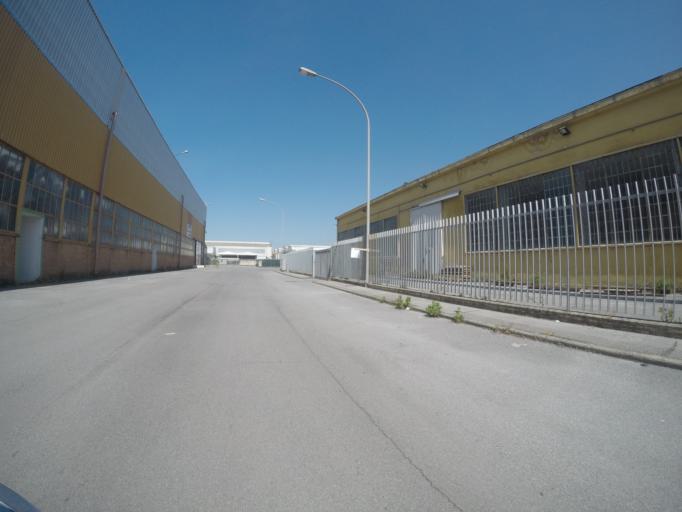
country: IT
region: Tuscany
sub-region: Provincia di Massa-Carrara
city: Massa
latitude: 44.0258
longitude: 10.1036
